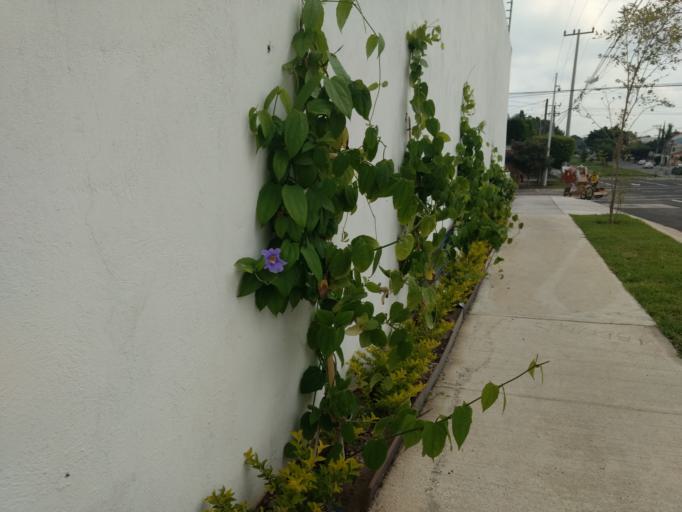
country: MX
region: Jalisco
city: Guadalajara
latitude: 20.6671
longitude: -103.4364
